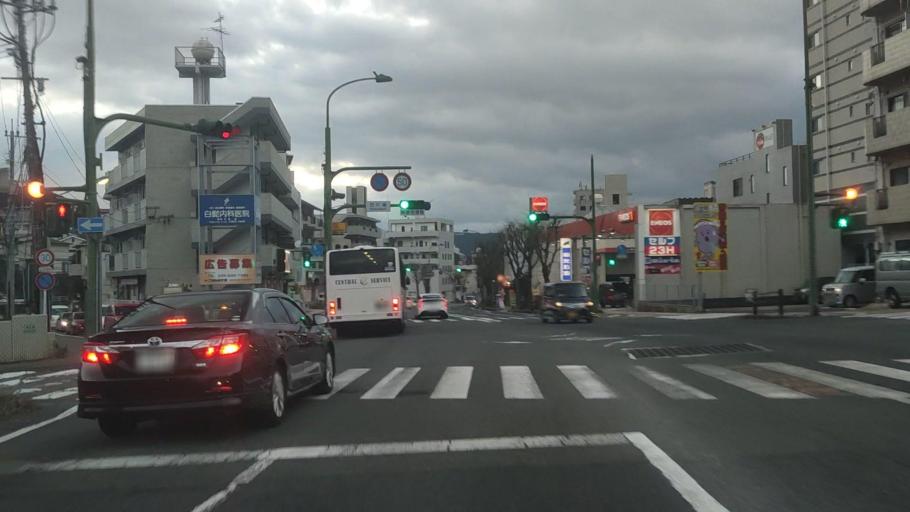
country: JP
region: Nagasaki
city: Nagasaki-shi
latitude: 32.7633
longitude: 129.8889
